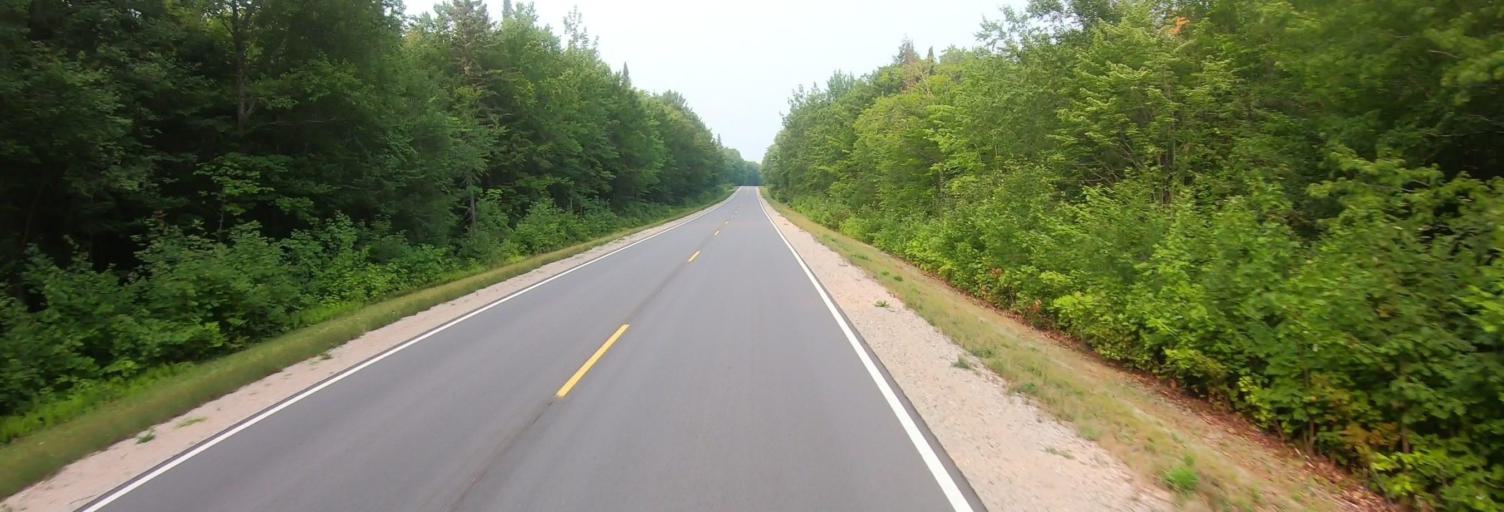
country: US
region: Michigan
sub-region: Luce County
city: Newberry
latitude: 46.4841
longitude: -85.0533
